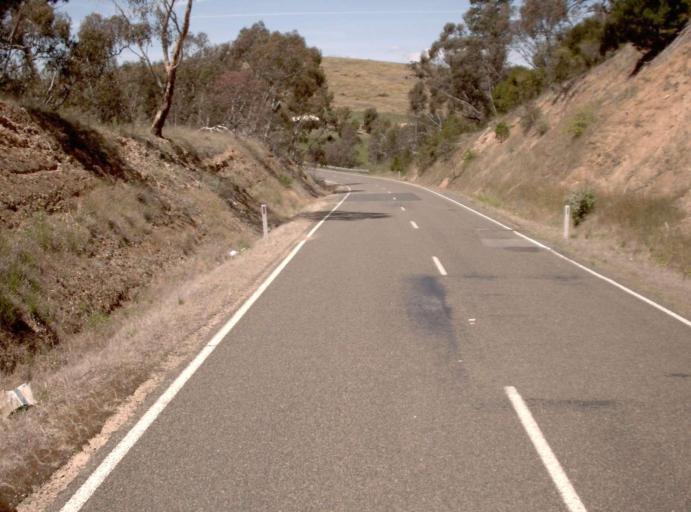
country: AU
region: Victoria
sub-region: Alpine
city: Mount Beauty
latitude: -37.1045
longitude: 147.6025
